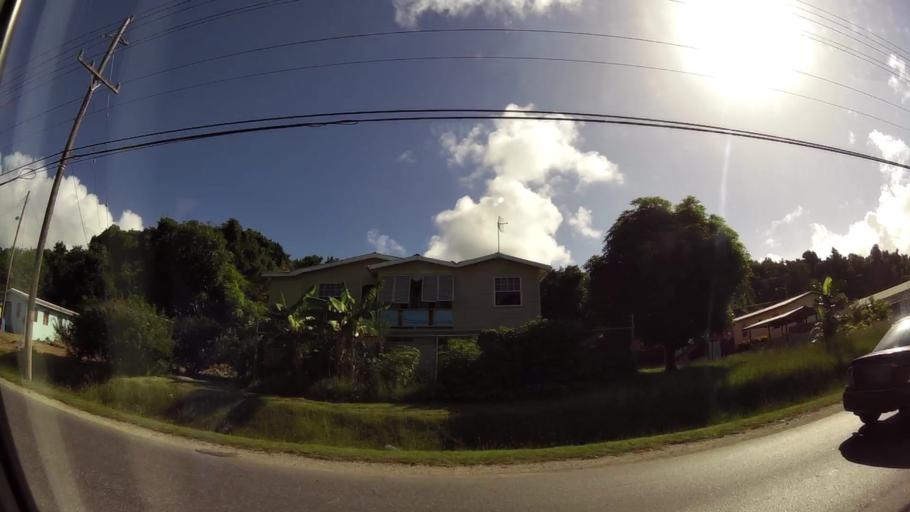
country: BB
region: Saint James
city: Holetown
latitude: 13.2117
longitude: -59.6176
